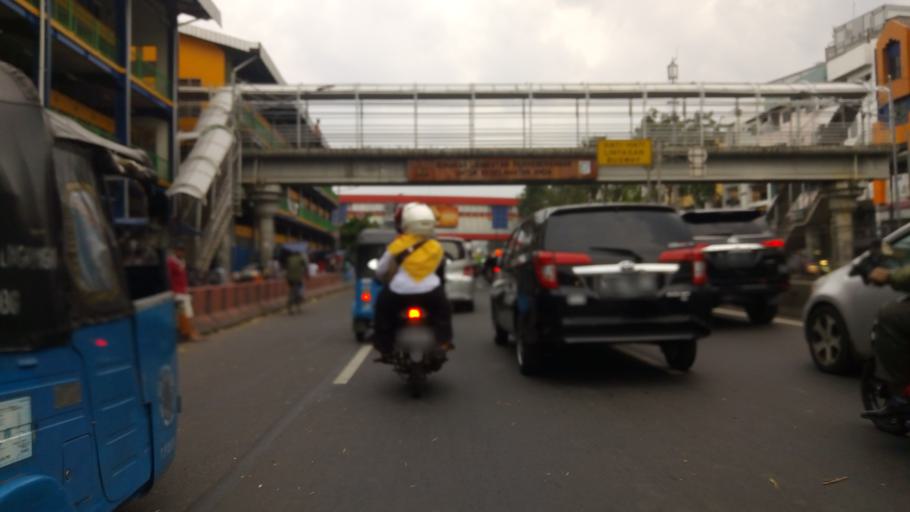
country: ID
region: Jakarta Raya
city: Jakarta
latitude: -6.1740
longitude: 106.8411
